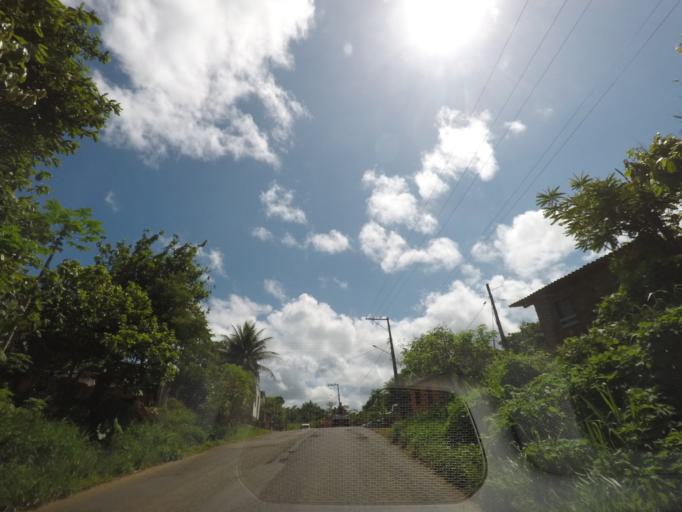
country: BR
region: Bahia
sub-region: Taperoa
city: Taperoa
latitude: -13.5250
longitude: -39.1033
